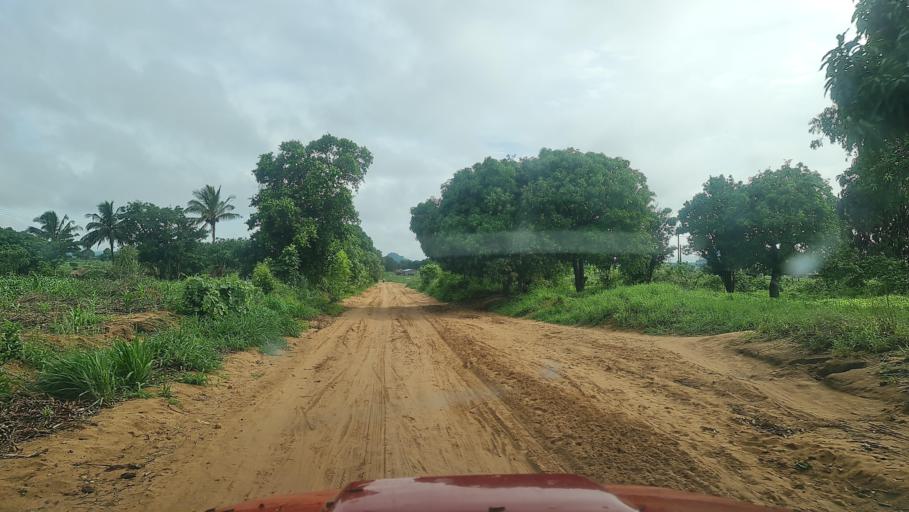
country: MW
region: Southern Region
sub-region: Nsanje District
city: Nsanje
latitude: -17.2803
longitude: 35.6160
